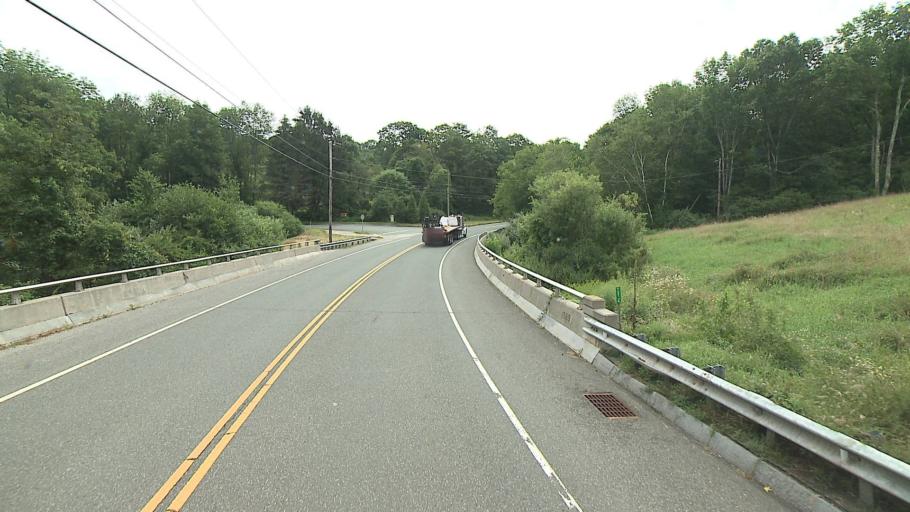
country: US
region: Connecticut
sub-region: Litchfield County
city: Bethlehem Village
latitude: 41.5964
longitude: -73.2593
